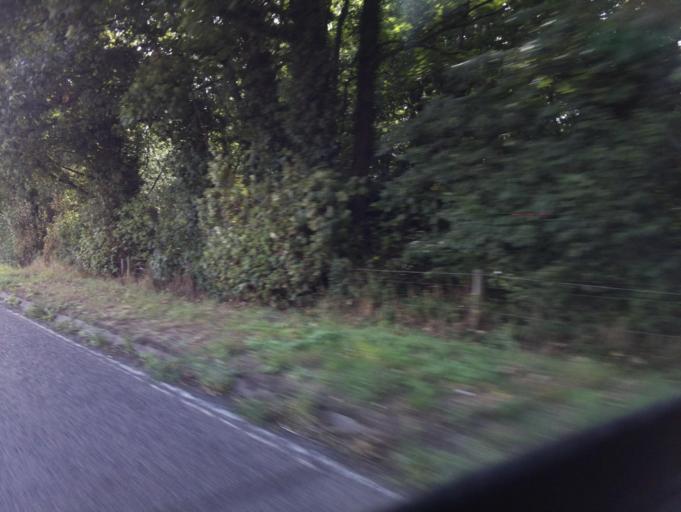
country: GB
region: England
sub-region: Leicestershire
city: Ashby de la Zouch
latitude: 52.7306
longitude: -1.4866
